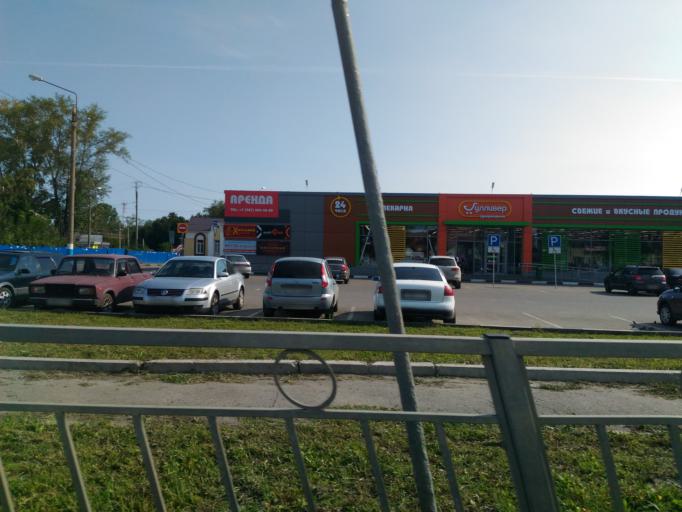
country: RU
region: Ulyanovsk
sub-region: Ulyanovskiy Rayon
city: Ulyanovsk
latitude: 54.3366
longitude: 48.5362
